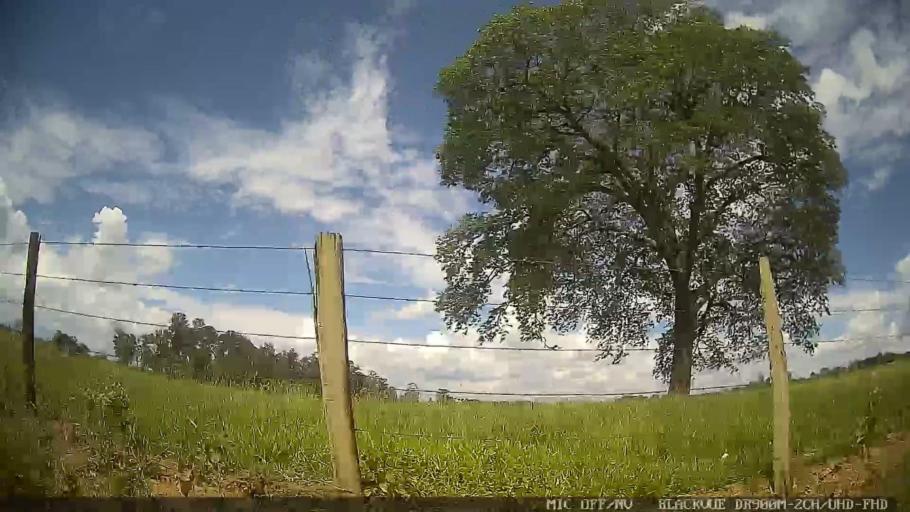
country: BR
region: Sao Paulo
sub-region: Conchas
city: Conchas
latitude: -23.0618
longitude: -47.9787
